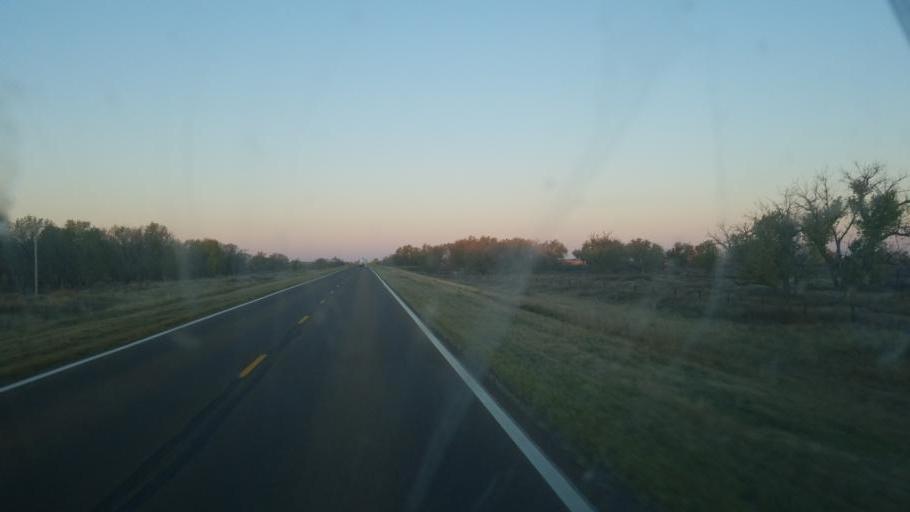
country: US
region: Kansas
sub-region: Wallace County
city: Sharon Springs
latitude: 38.9021
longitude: -101.6891
